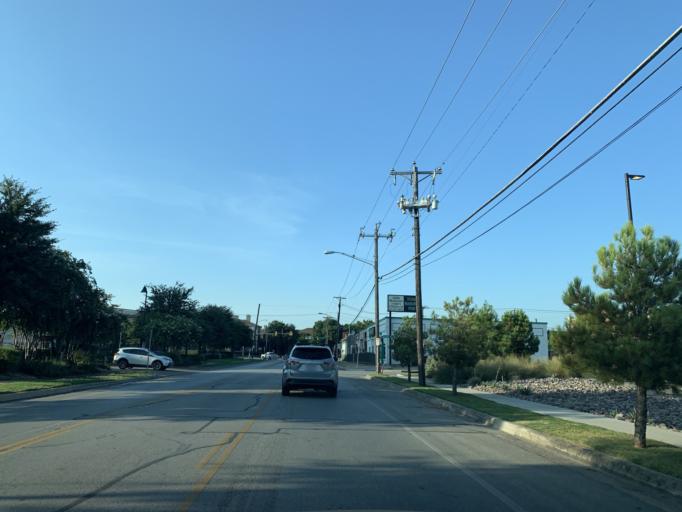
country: US
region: Texas
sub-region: Tarrant County
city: Fort Worth
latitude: 32.7525
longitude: -97.3548
